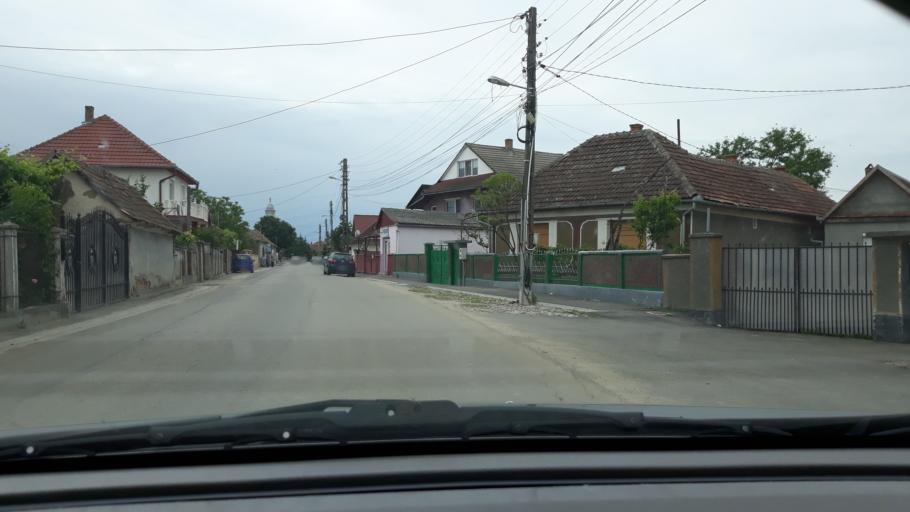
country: RO
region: Bihor
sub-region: Comuna Osorheiu
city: Osorheiu
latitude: 47.0585
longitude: 22.0435
